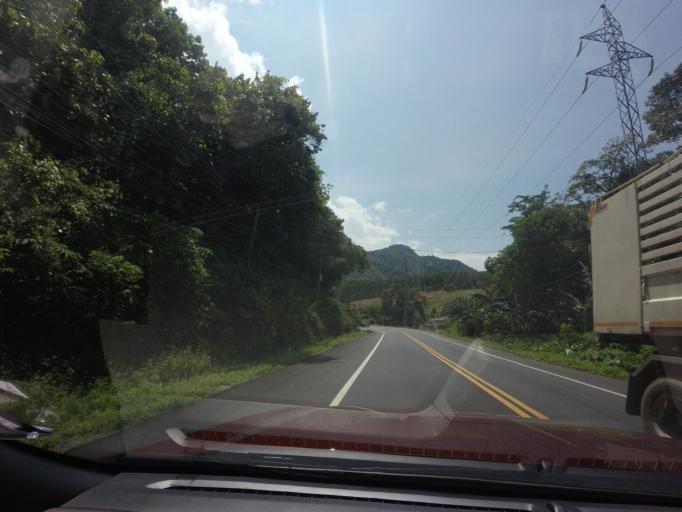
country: TH
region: Yala
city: Than To
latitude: 5.9803
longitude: 101.2001
